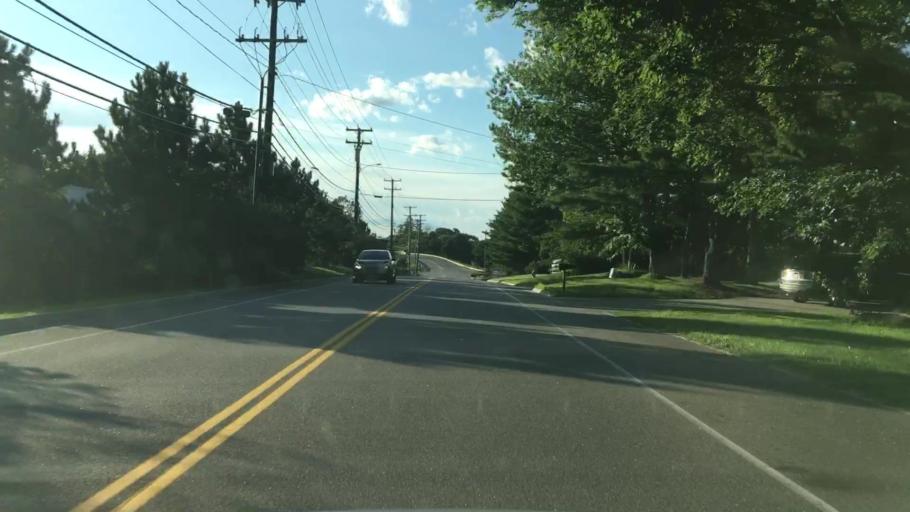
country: US
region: Maine
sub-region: Cumberland County
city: Scarborough
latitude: 43.6005
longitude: -70.2989
